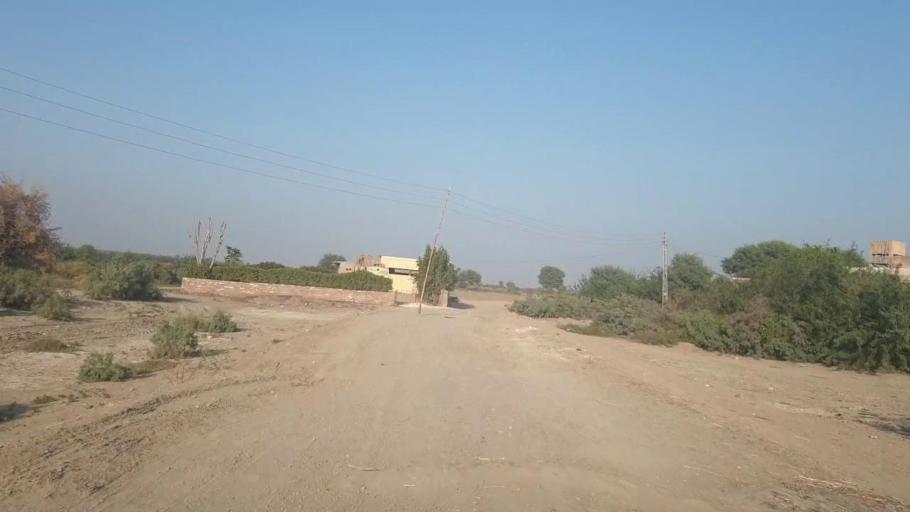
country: PK
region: Sindh
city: Jamshoro
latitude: 25.4181
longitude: 68.3035
